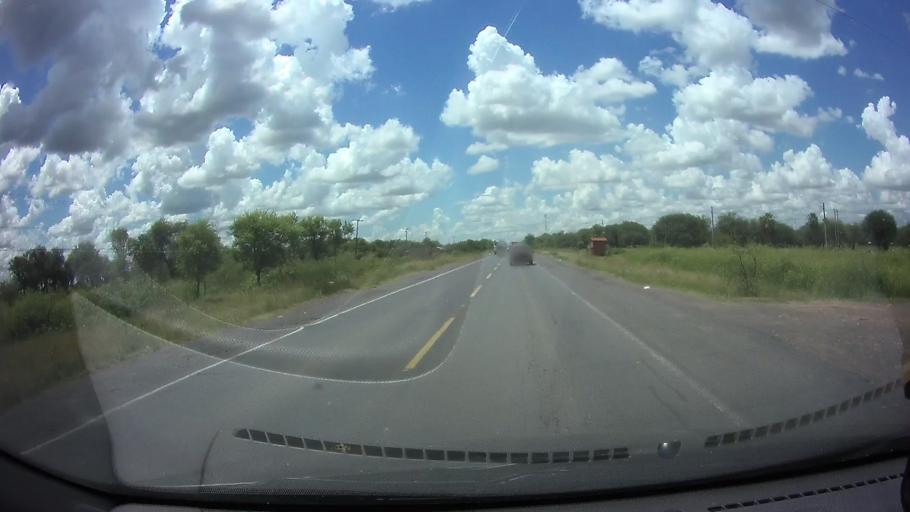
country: PY
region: Presidente Hayes
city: Nanawa
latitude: -25.2283
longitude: -57.6890
